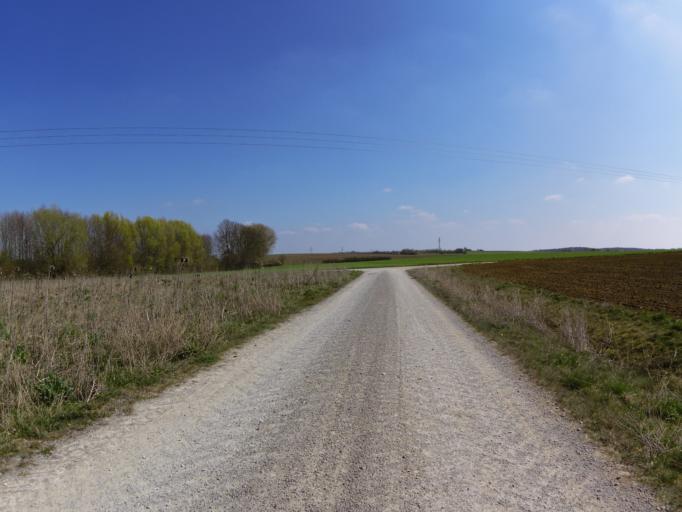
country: DE
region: Bavaria
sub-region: Regierungsbezirk Unterfranken
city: Biebelried
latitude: 49.7405
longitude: 10.0871
